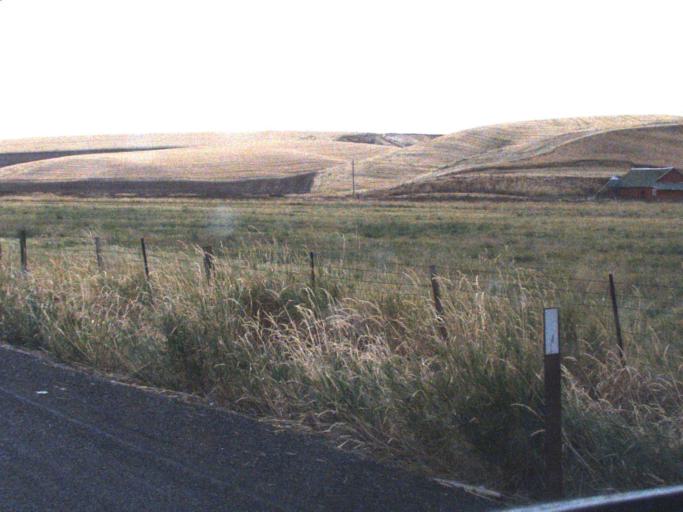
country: US
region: Washington
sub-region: Whitman County
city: Colfax
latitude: 46.8053
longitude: -117.5703
